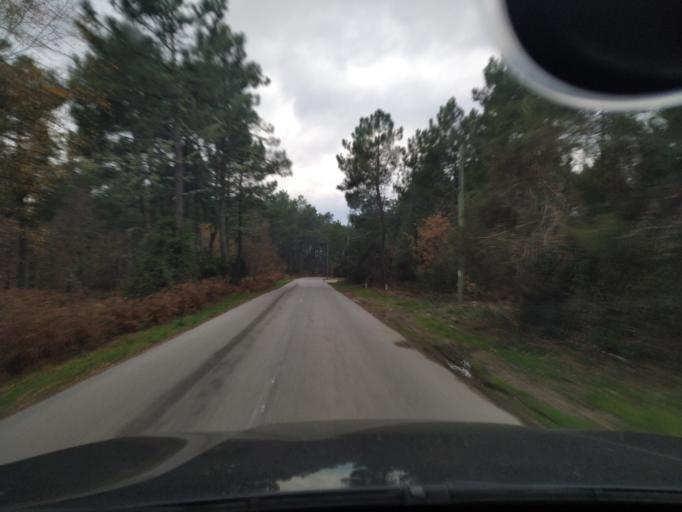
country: PT
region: Vila Real
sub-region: Vila Real
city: Vila Real
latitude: 41.3373
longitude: -7.6541
